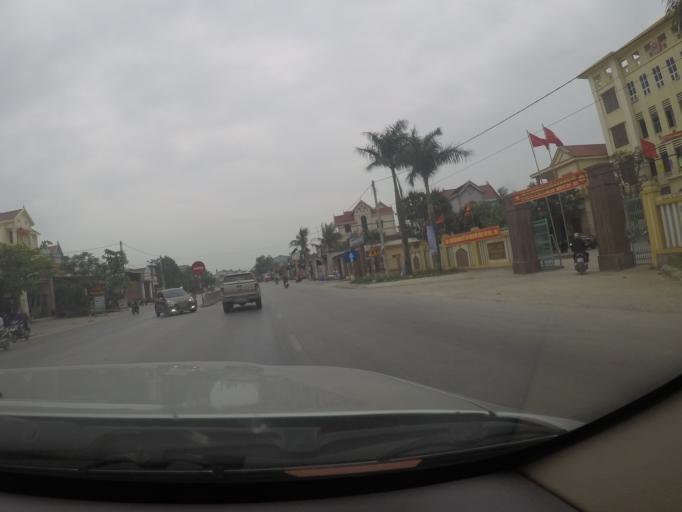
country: VN
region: Nghe An
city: Dien Chau
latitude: 19.0146
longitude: 105.5861
